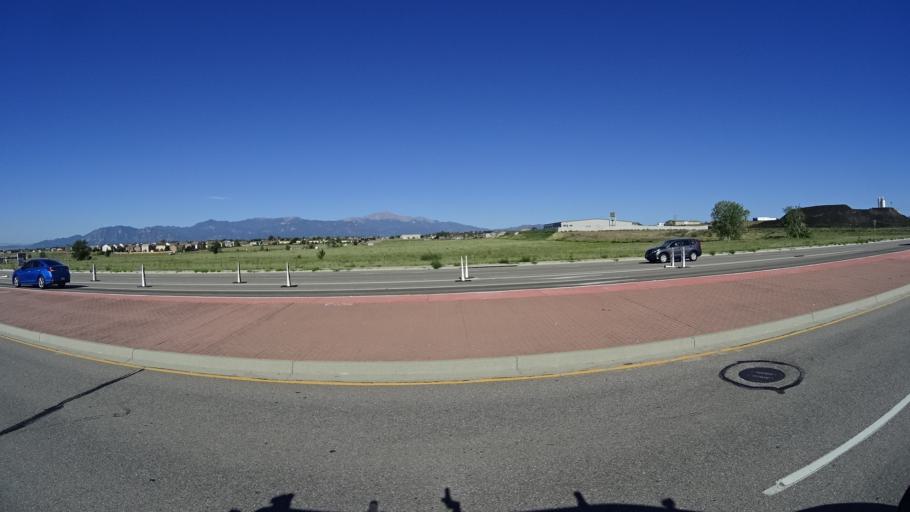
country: US
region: Colorado
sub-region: El Paso County
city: Cimarron Hills
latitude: 38.8693
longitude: -104.6826
